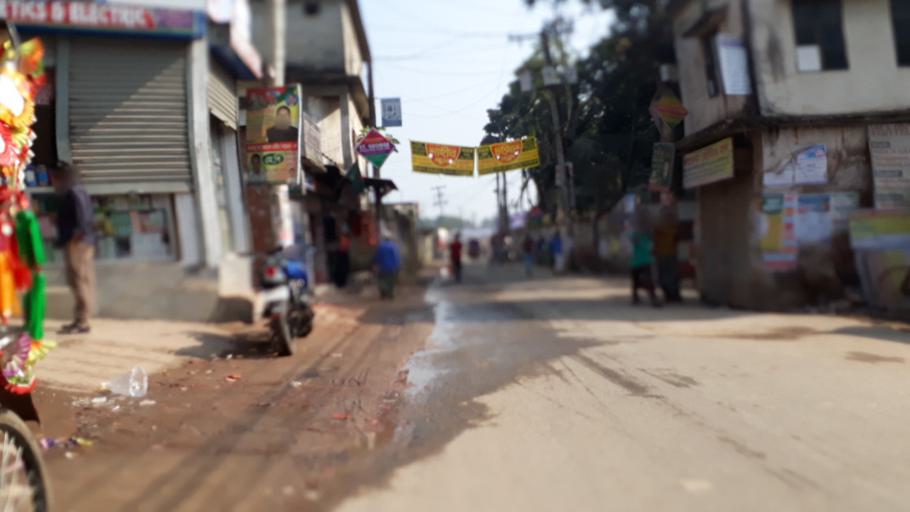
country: BD
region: Dhaka
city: Tungi
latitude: 23.8482
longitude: 90.2660
